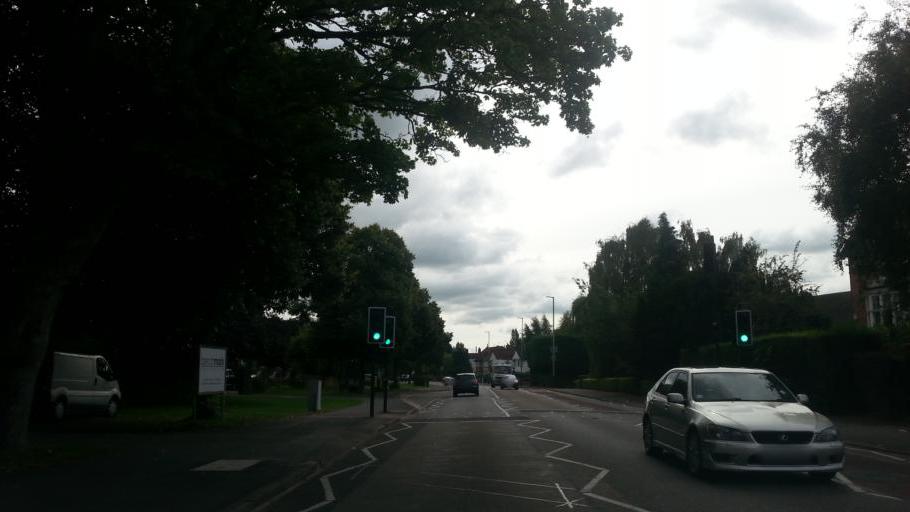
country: GB
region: England
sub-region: Leicestershire
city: Oadby
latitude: 52.6090
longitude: -1.0991
